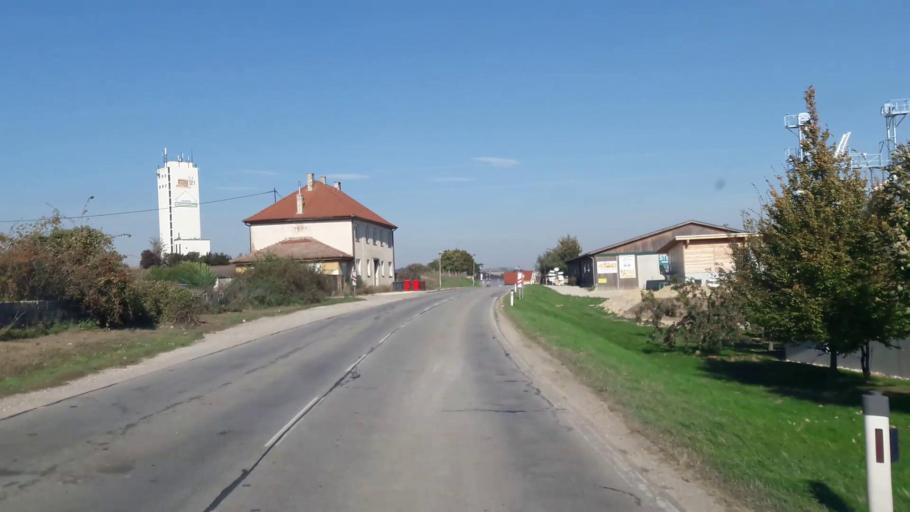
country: AT
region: Lower Austria
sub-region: Politischer Bezirk Korneuburg
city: Grossrussbach
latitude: 48.4733
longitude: 16.3802
